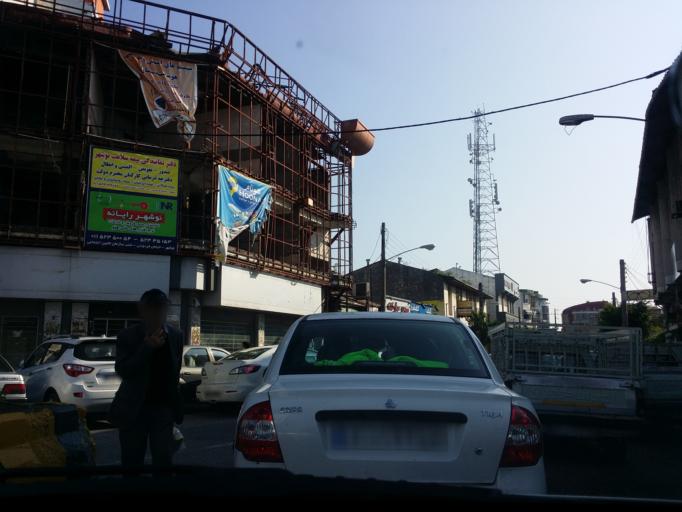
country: IR
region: Mazandaran
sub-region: Nowshahr
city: Nowshahr
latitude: 36.6508
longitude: 51.5056
